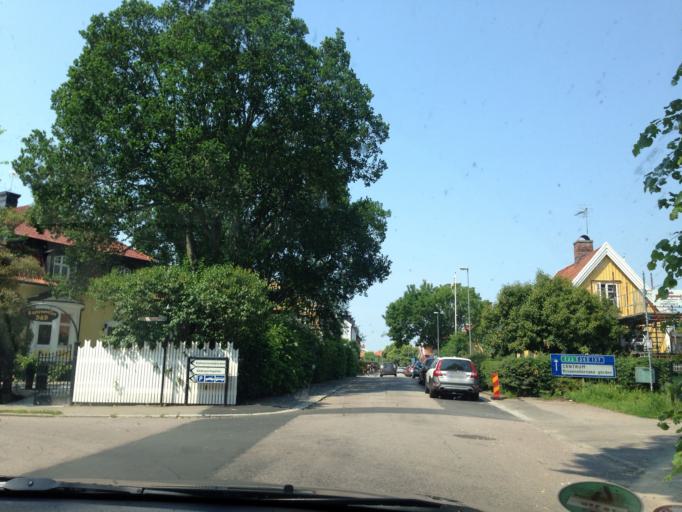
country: SE
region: Kalmar
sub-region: Kalmar Kommun
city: Kalmar
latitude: 56.6595
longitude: 16.3518
